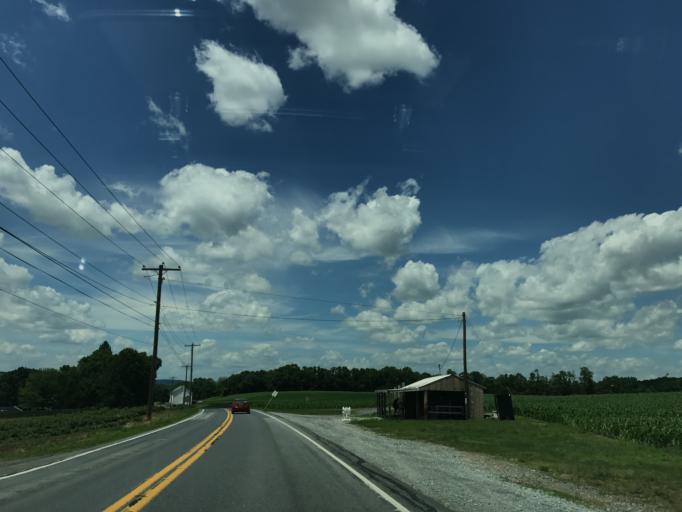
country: US
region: Pennsylvania
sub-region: Lancaster County
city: Mountville
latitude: 39.9769
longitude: -76.4588
